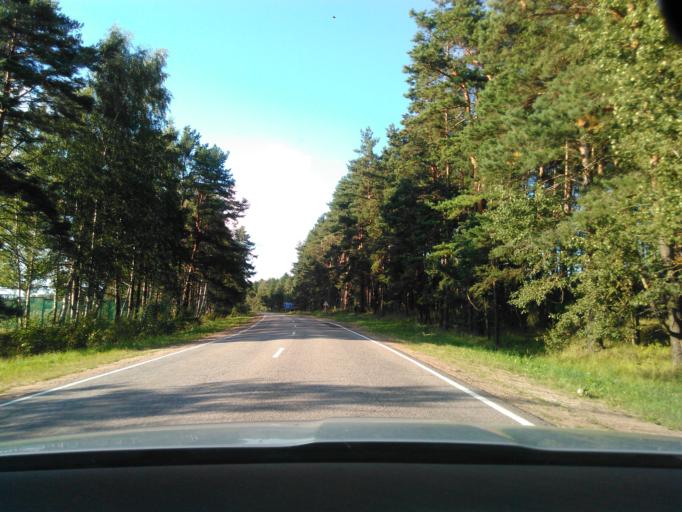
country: RU
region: Tverskaya
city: Zavidovo
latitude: 56.5889
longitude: 36.5410
